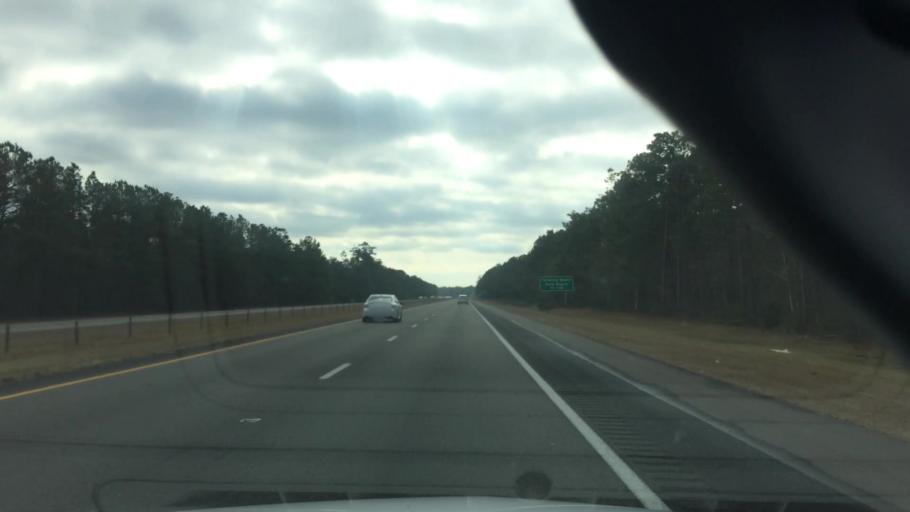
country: US
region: North Carolina
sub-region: New Hanover County
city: Castle Hayne
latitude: 34.3844
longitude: -77.8791
